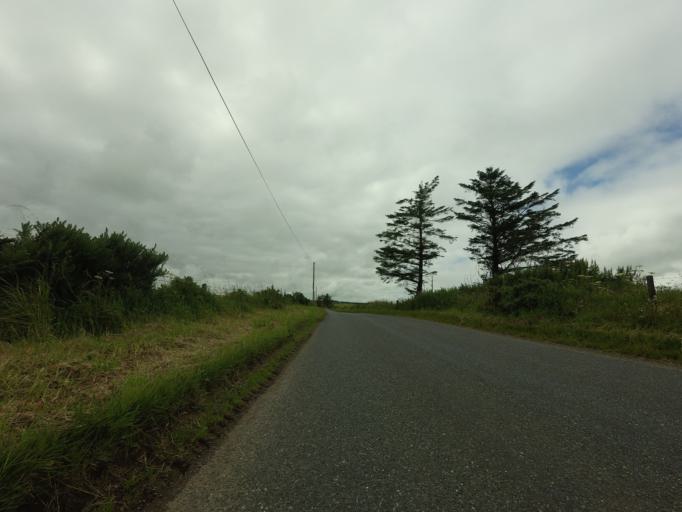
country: GB
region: Scotland
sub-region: Aberdeenshire
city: Rosehearty
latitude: 57.5417
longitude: -2.2063
